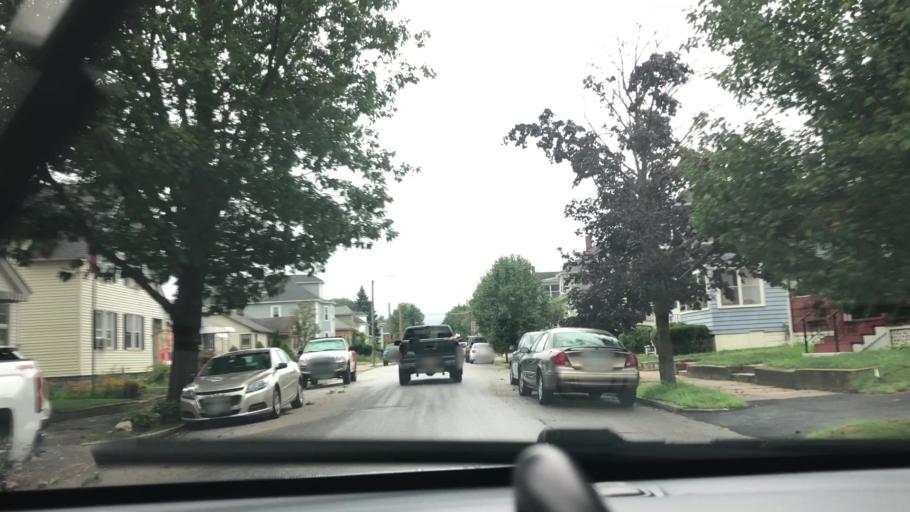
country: US
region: New Hampshire
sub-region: Hillsborough County
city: Manchester
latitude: 42.9987
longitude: -71.4809
